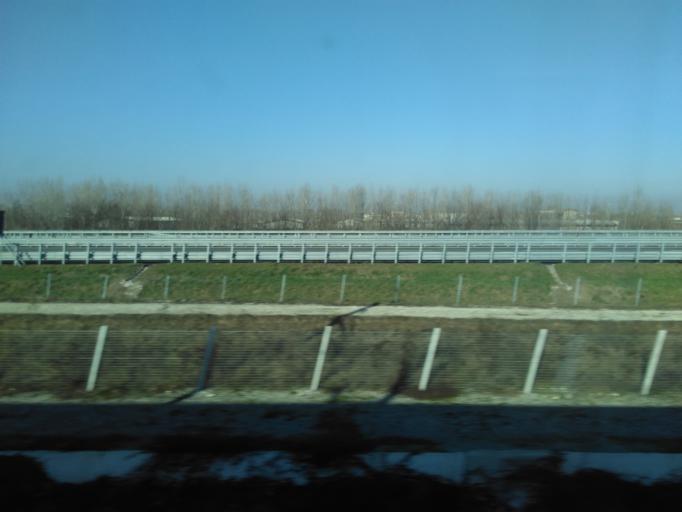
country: IT
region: Lombardy
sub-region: Provincia di Brescia
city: Rudiano
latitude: 45.5029
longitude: 9.8791
